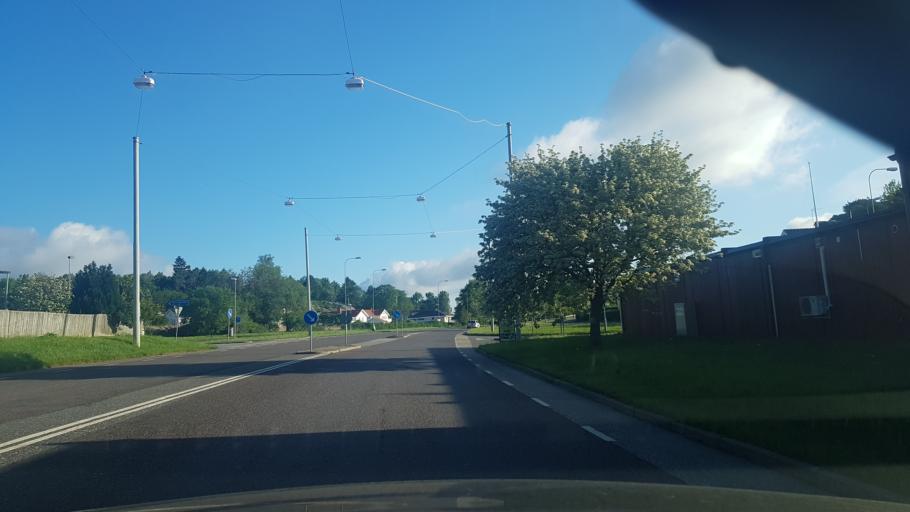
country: SE
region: Vaestra Goetaland
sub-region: Goteborg
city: Majorna
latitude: 57.6427
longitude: 11.8807
